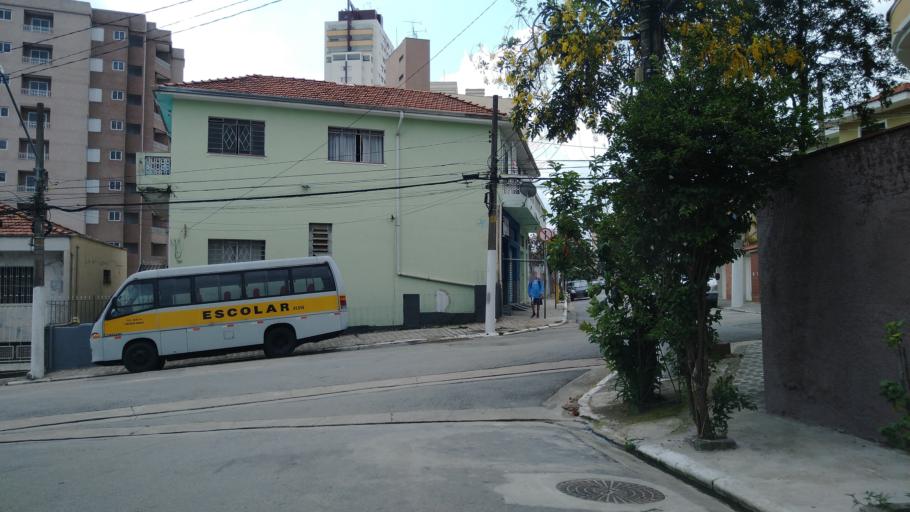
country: BR
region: Sao Paulo
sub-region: Sao Paulo
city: Sao Paulo
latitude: -23.4890
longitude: -46.6045
